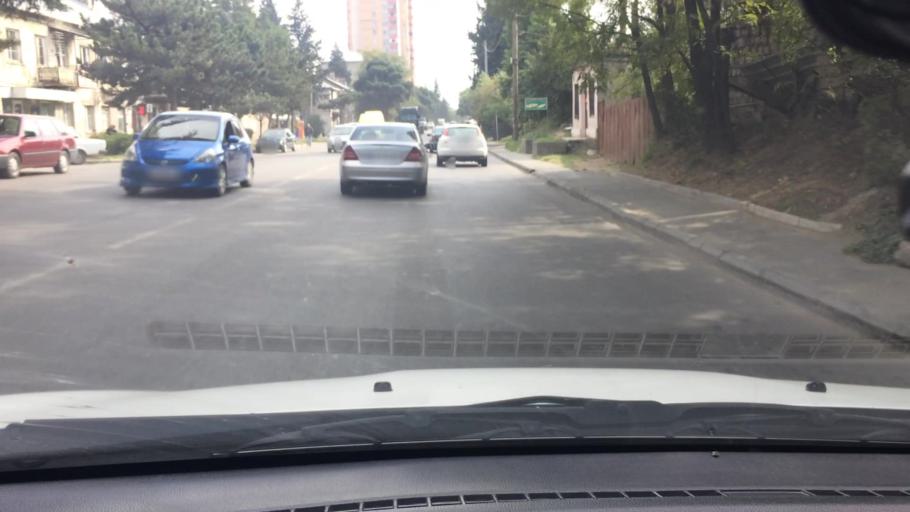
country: GE
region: T'bilisi
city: Tbilisi
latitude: 41.6511
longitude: 44.9071
